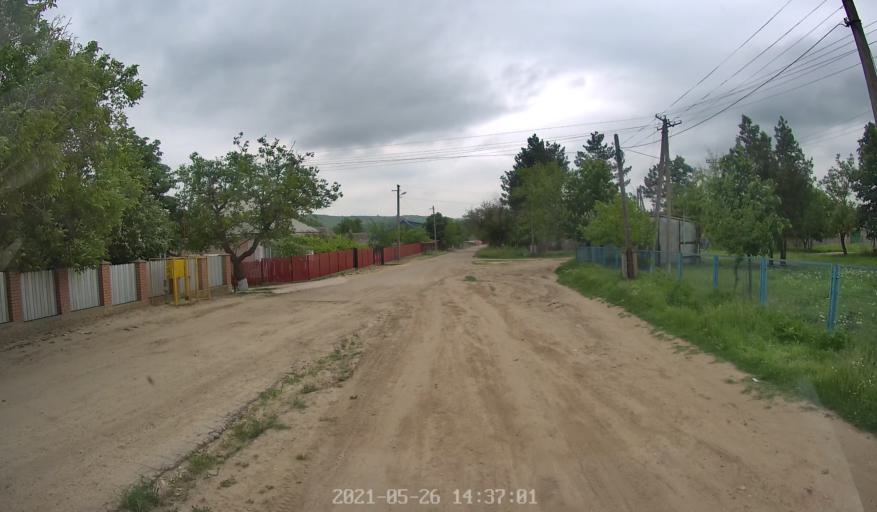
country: MD
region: Hincesti
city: Dancu
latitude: 46.6757
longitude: 28.3299
